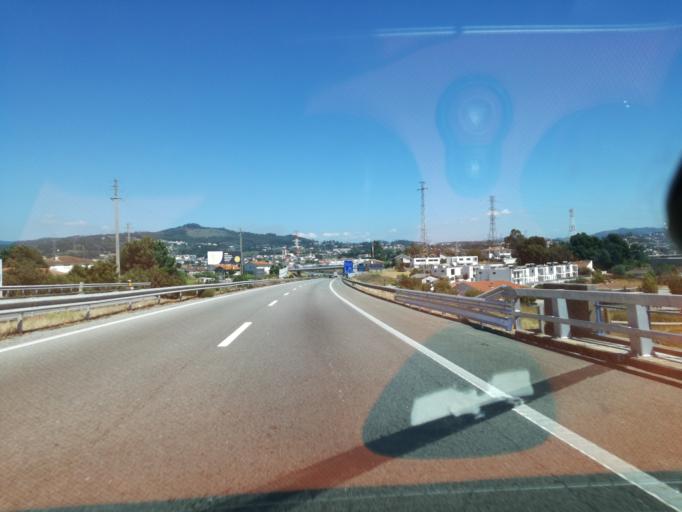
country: PT
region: Braga
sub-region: Guimaraes
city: Serzedelo
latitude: 41.4071
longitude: -8.3950
